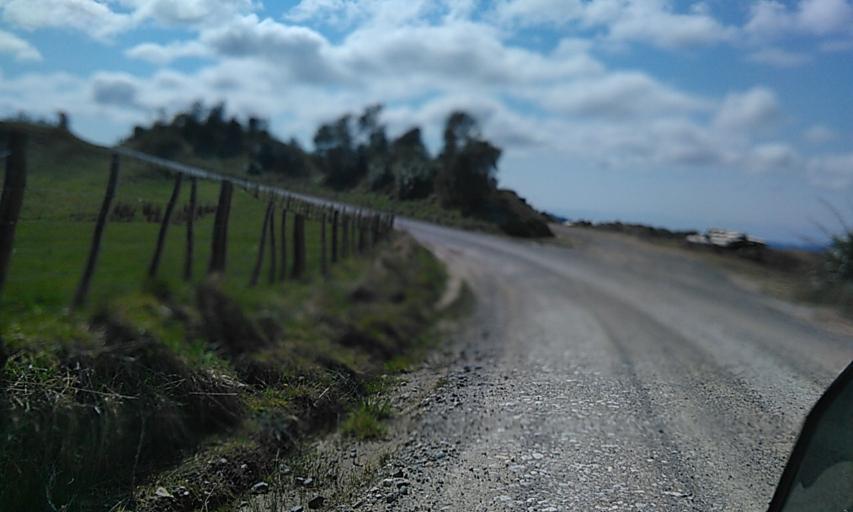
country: NZ
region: Gisborne
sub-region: Gisborne District
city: Gisborne
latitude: -38.2258
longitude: 178.0698
